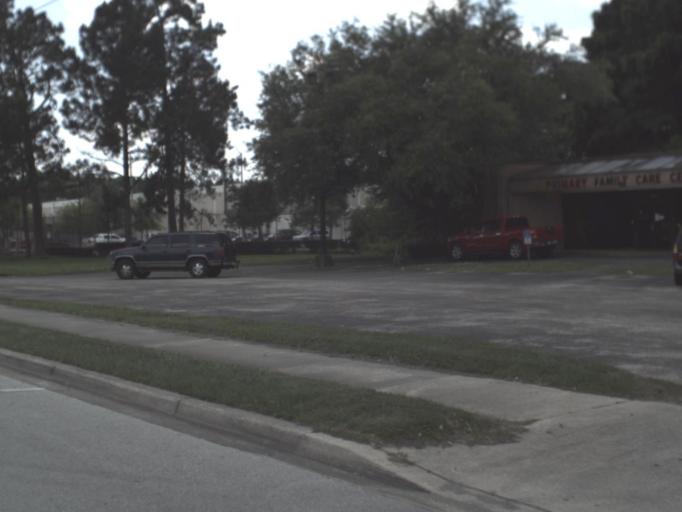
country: US
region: Florida
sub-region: Duval County
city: Jacksonville
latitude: 30.3461
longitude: -81.7312
